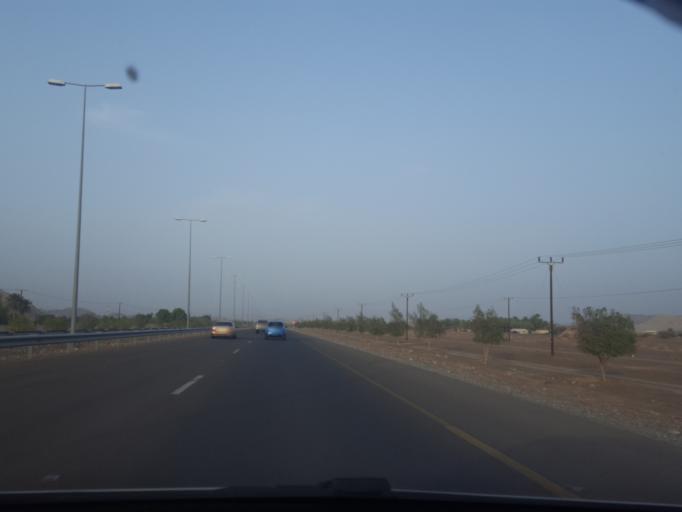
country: OM
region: Al Buraimi
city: Al Buraymi
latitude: 24.2419
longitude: 55.9747
